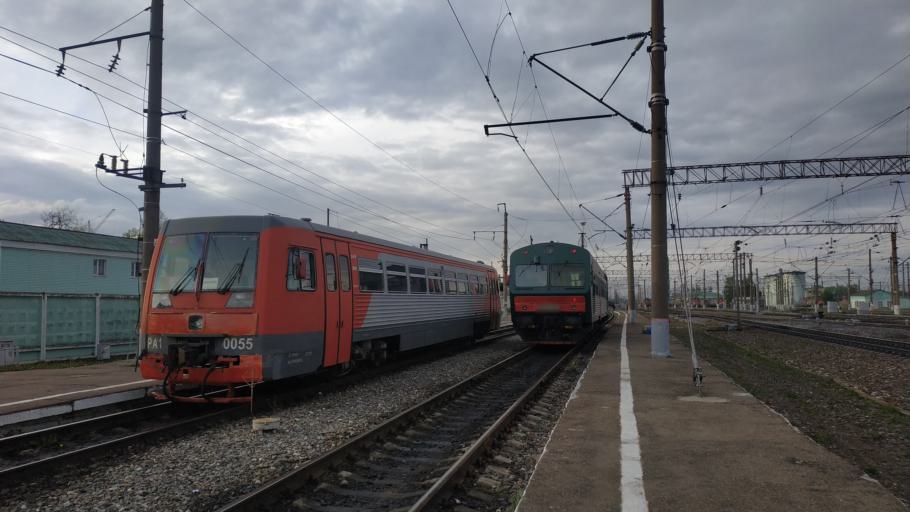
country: RU
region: Smolensk
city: Vyaz'ma
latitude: 55.2003
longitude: 34.3191
